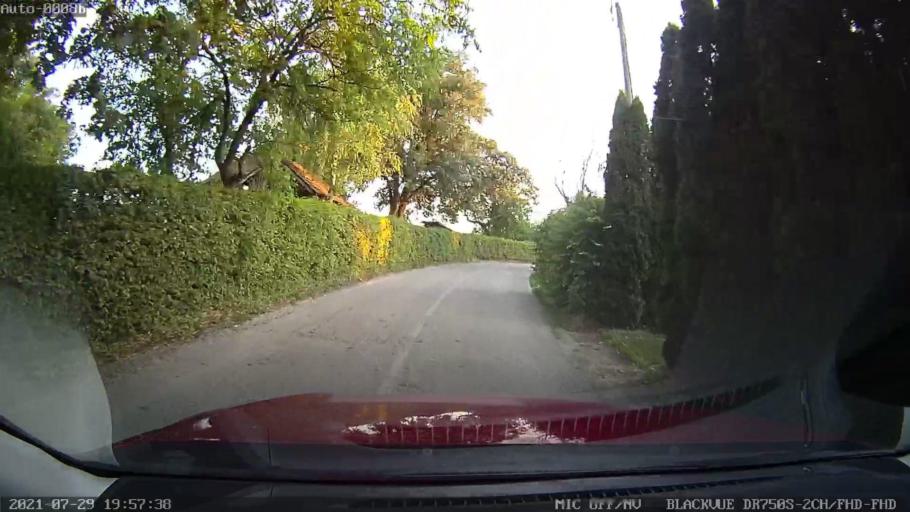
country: HR
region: Varazdinska
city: Jalzabet
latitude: 46.2415
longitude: 16.4751
